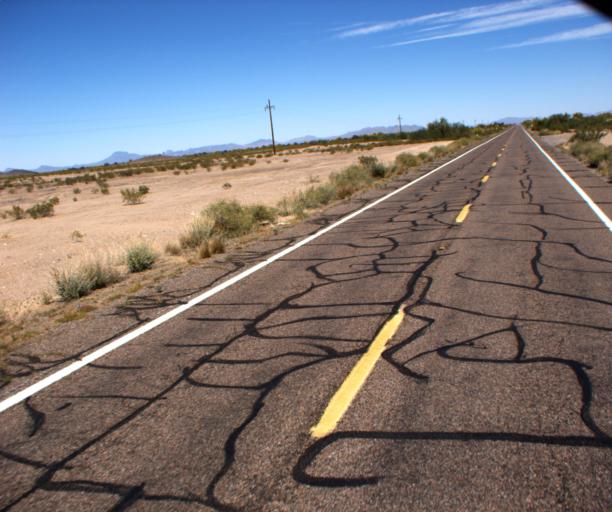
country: US
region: Arizona
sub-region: Maricopa County
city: Gila Bend
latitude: 32.8003
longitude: -112.7994
